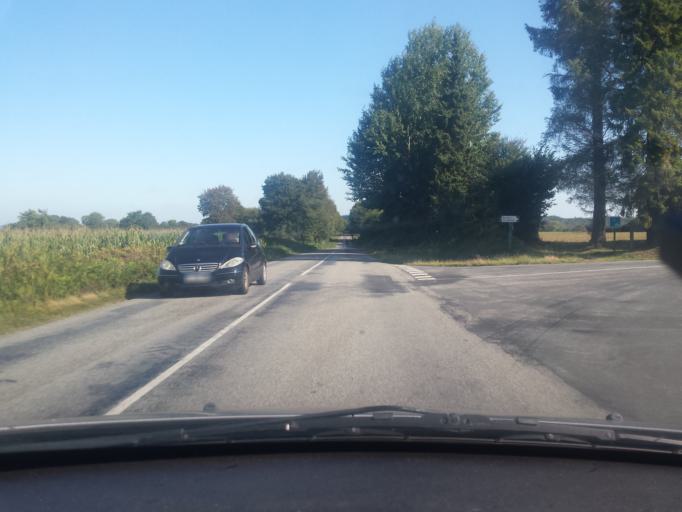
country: FR
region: Brittany
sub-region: Departement du Morbihan
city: Cleguerec
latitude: 48.1011
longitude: -3.1008
